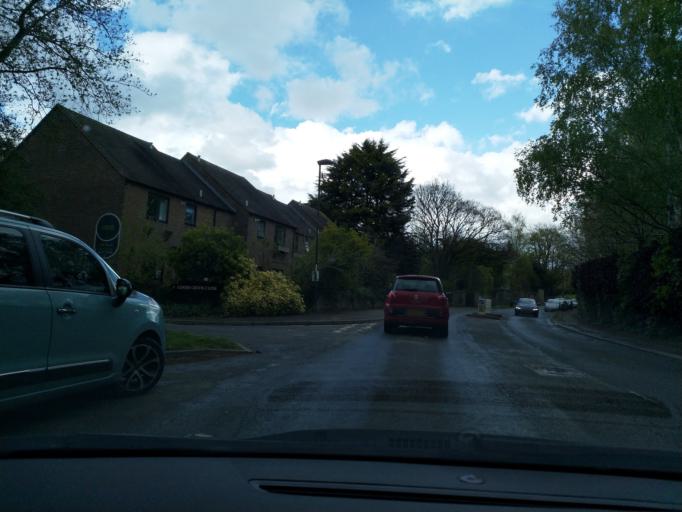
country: GB
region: England
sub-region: Oxfordshire
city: Yarnton
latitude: 51.7858
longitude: -1.2843
